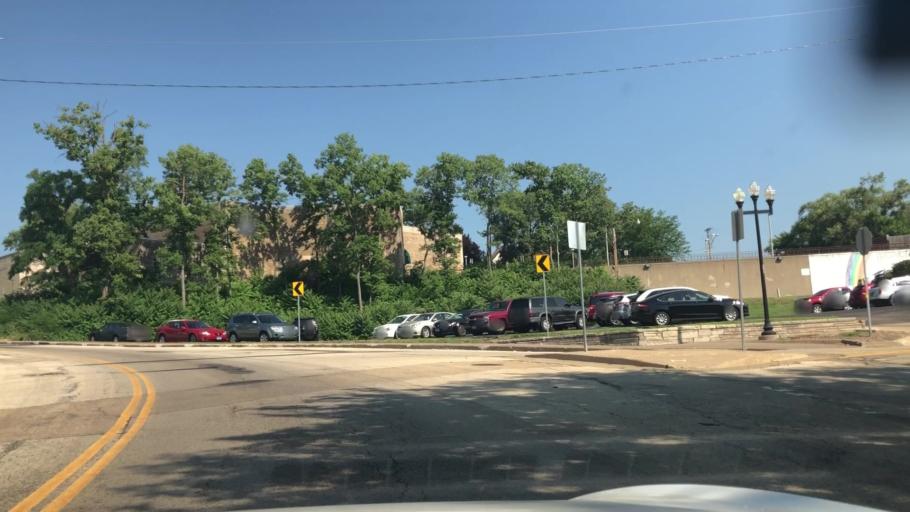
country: US
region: Illinois
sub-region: Peoria County
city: Peoria
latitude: 40.6995
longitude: -89.5976
